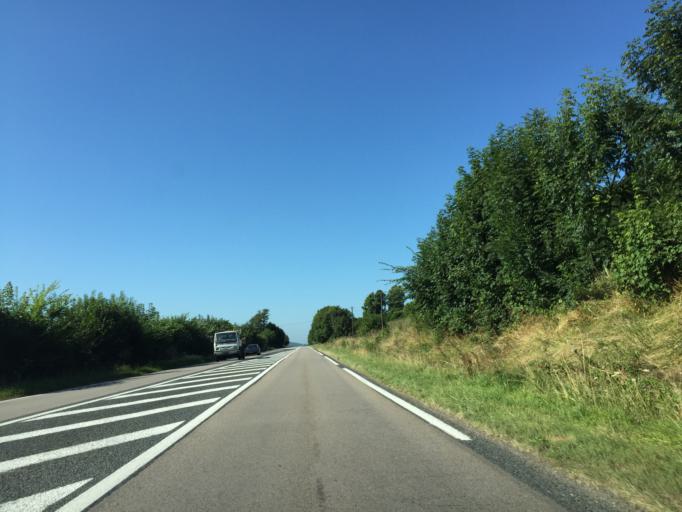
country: FR
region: Lower Normandy
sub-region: Departement du Calvados
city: Lisieux
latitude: 49.1702
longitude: 0.2274
